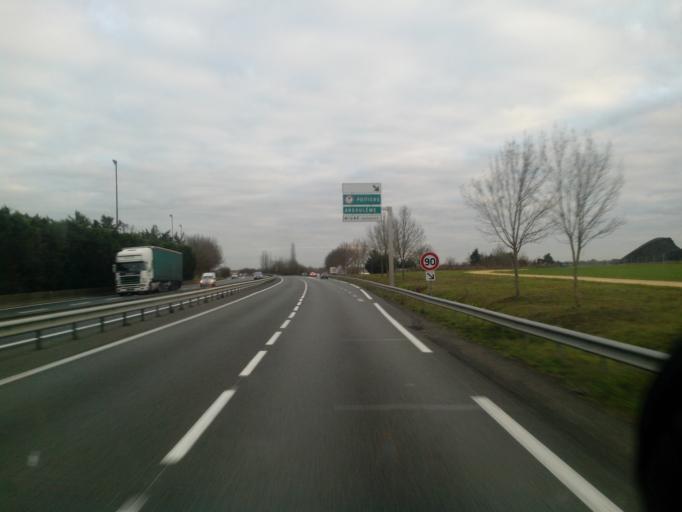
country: FR
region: Poitou-Charentes
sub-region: Departement de la Vienne
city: Migne-Auxances
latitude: 46.6190
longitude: 0.3072
